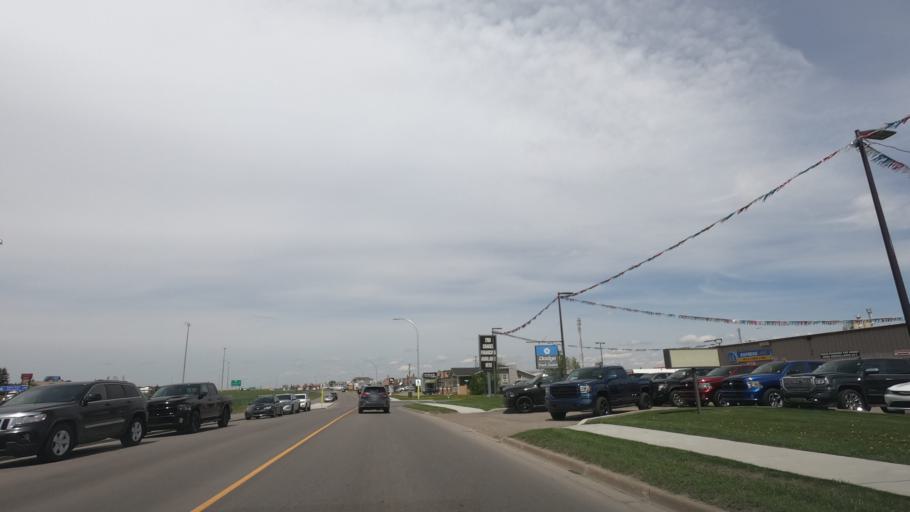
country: CA
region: Alberta
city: Airdrie
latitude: 51.2894
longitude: -113.9991
